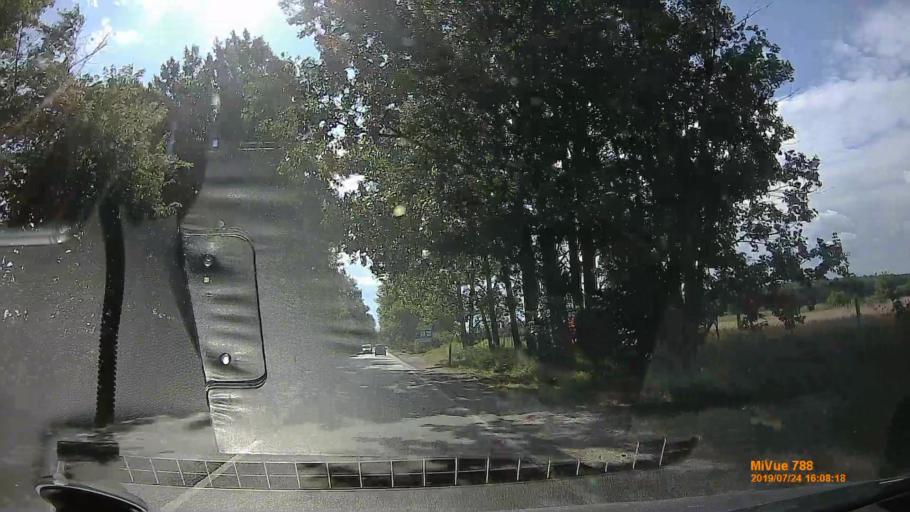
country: HU
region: Szabolcs-Szatmar-Bereg
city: Napkor
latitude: 47.9551
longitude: 21.8955
